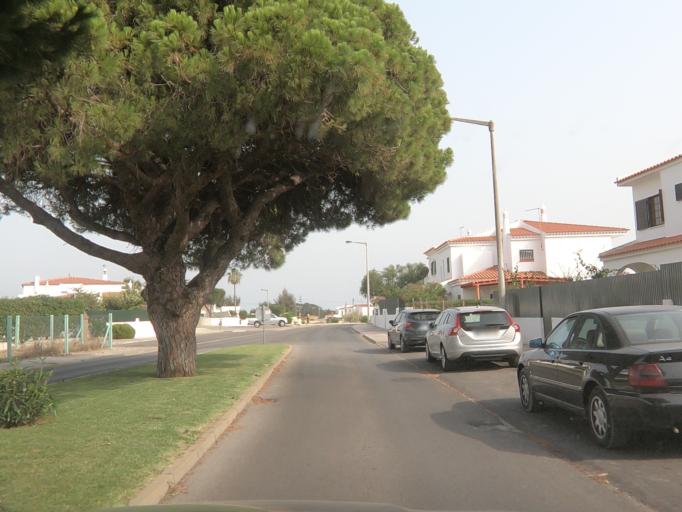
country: PT
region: Faro
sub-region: Albufeira
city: Guia
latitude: 37.0813
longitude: -8.3079
